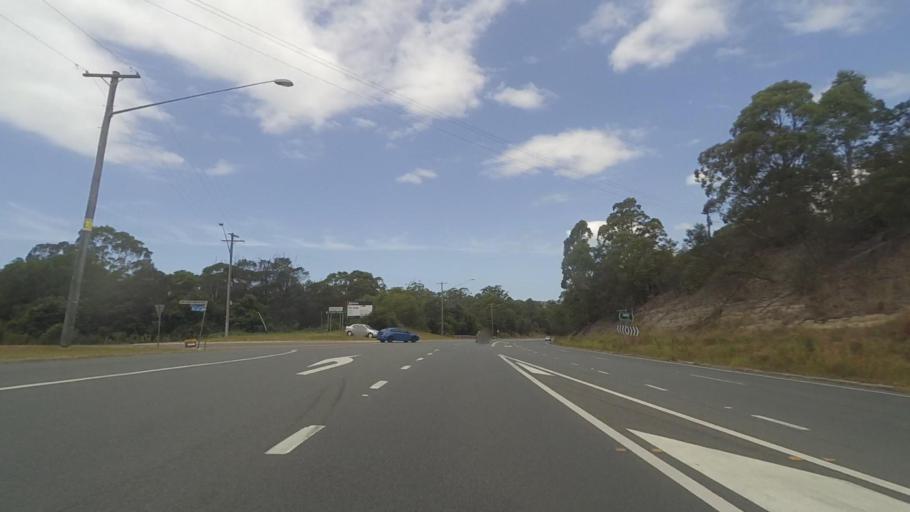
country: AU
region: New South Wales
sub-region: Shoalhaven Shire
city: Milton
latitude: -35.2588
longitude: 150.4278
